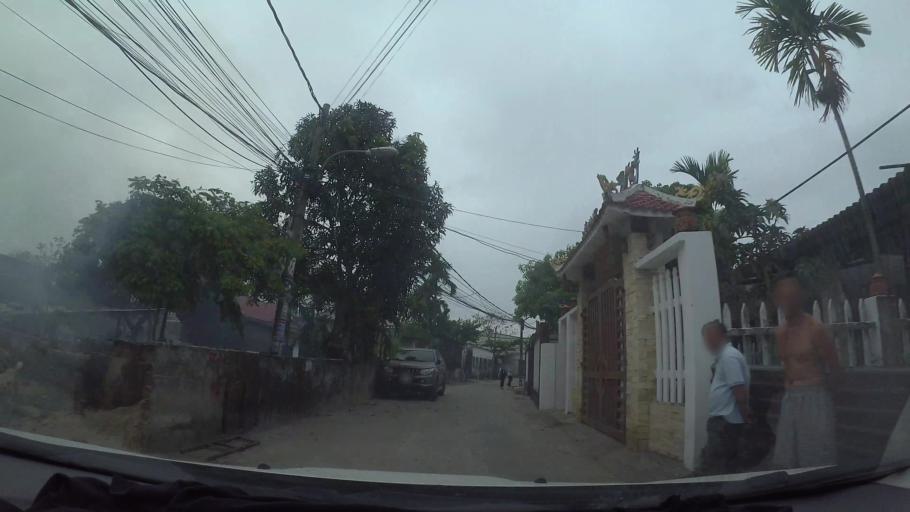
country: VN
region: Da Nang
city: Lien Chieu
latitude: 16.0848
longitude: 108.1567
